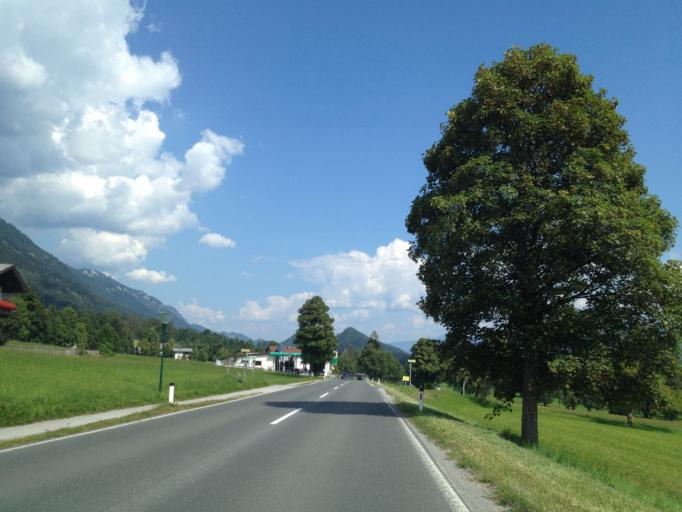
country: AT
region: Styria
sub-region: Politischer Bezirk Liezen
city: Schladming
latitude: 47.4205
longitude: 13.6604
